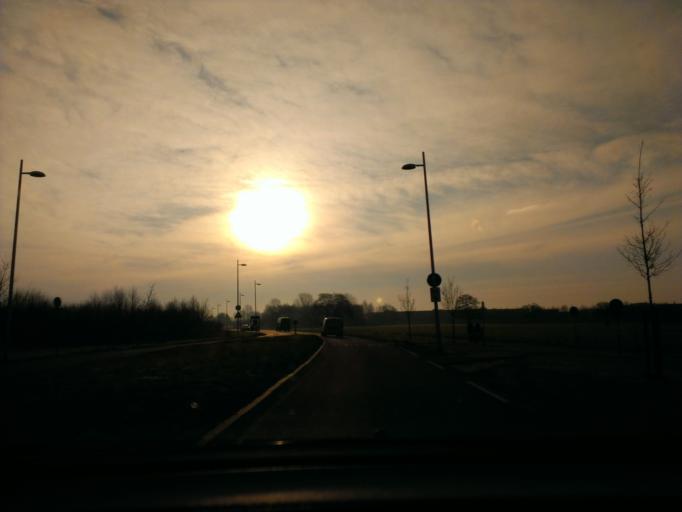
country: NL
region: Gelderland
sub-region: Gemeente Apeldoorn
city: Apeldoorn
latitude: 52.2467
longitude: 5.9801
